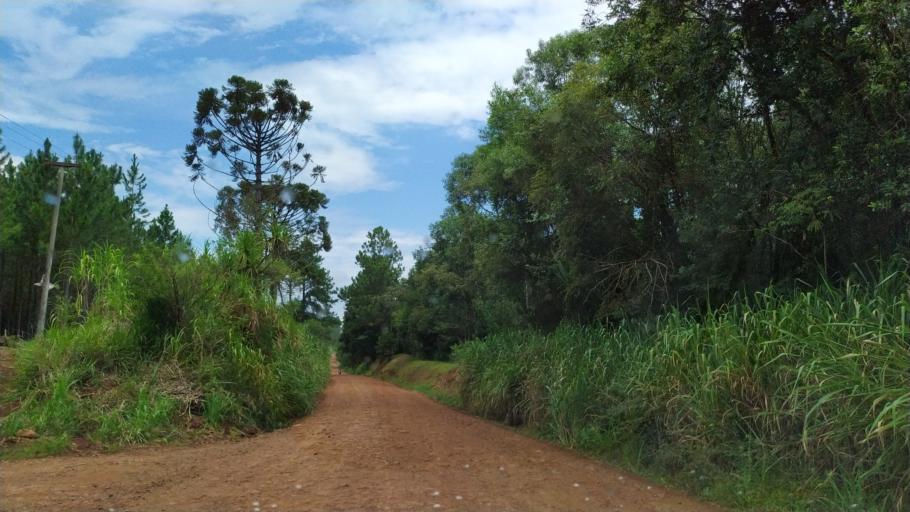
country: AR
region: Misiones
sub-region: Departamento de Eldorado
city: Eldorado
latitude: -26.4358
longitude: -54.6045
